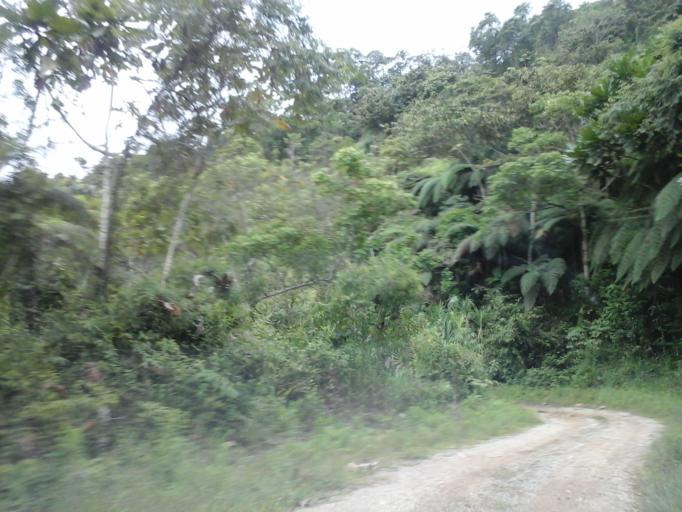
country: CO
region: Antioquia
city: San Roque
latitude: 6.5014
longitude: -74.9768
